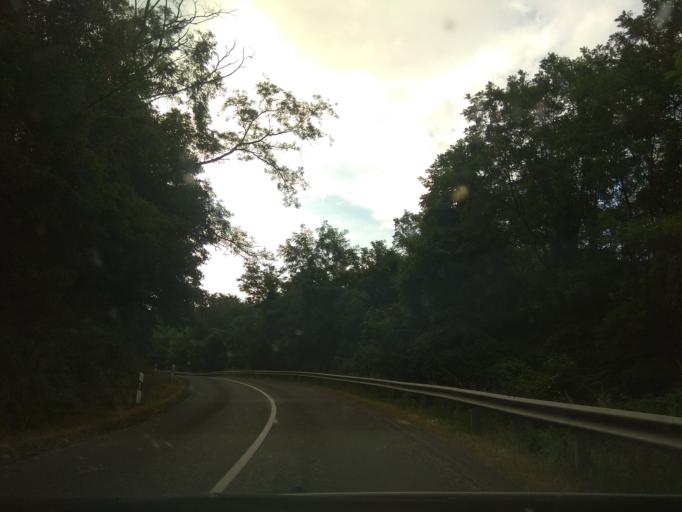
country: HU
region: Heves
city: Tarnalelesz
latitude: 48.0541
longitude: 20.2144
